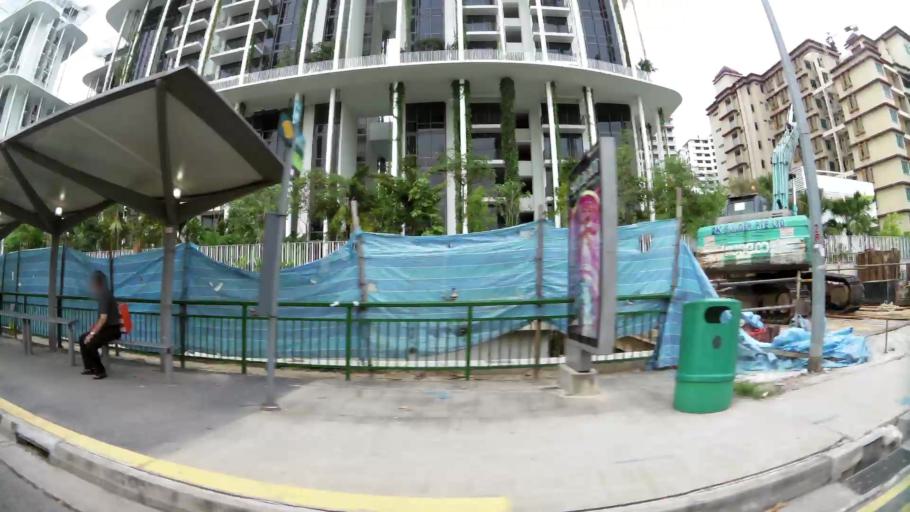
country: SG
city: Singapore
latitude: 1.3614
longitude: 103.8904
